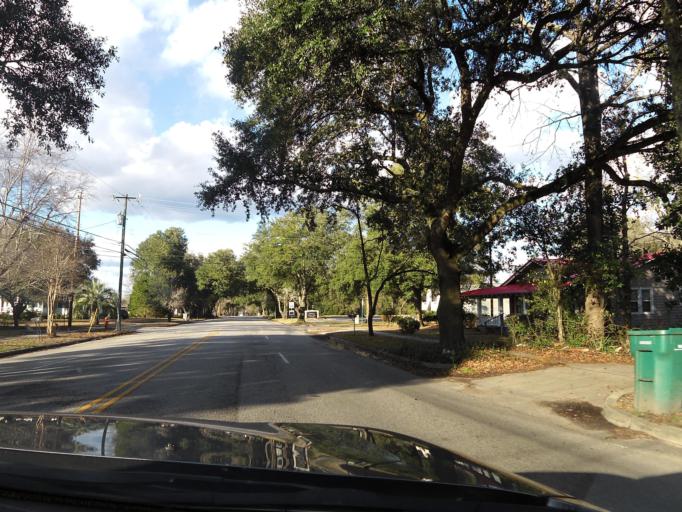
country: US
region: South Carolina
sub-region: Clarendon County
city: Manning
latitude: 33.7006
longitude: -80.2089
